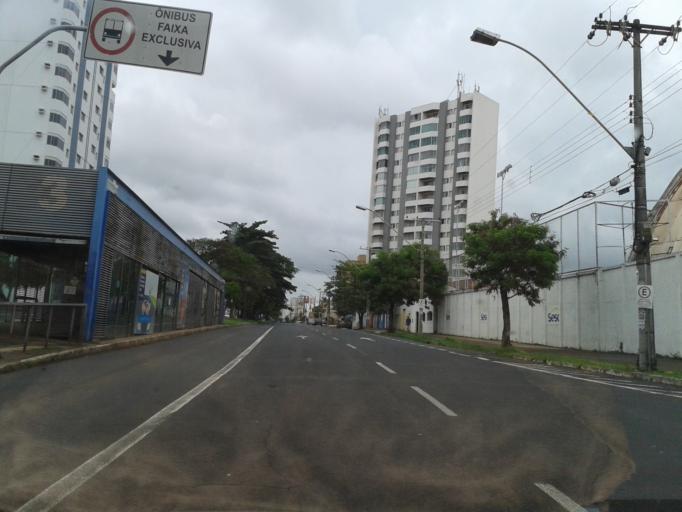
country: BR
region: Minas Gerais
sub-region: Uberlandia
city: Uberlandia
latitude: -18.9118
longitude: -48.2652
